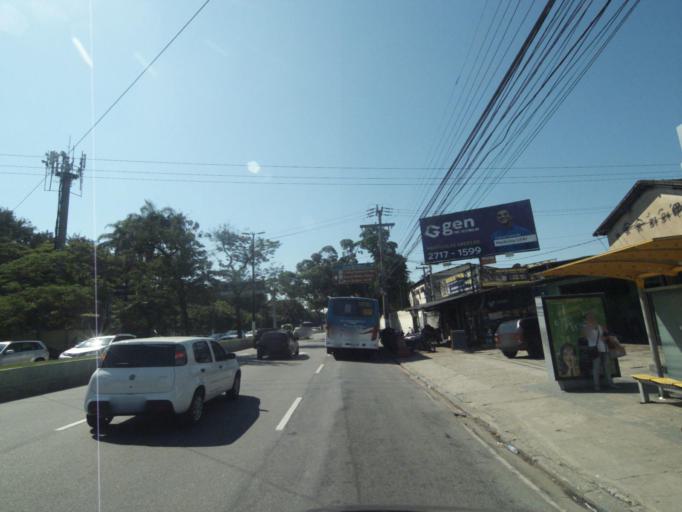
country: BR
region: Rio de Janeiro
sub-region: Niteroi
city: Niteroi
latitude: -22.8871
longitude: -43.1149
